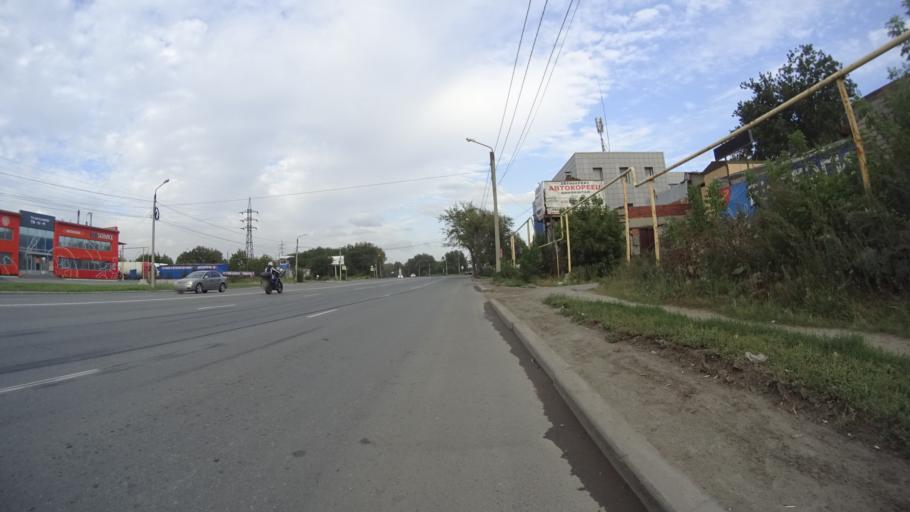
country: RU
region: Chelyabinsk
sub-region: Gorod Chelyabinsk
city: Chelyabinsk
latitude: 55.1920
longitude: 61.4294
